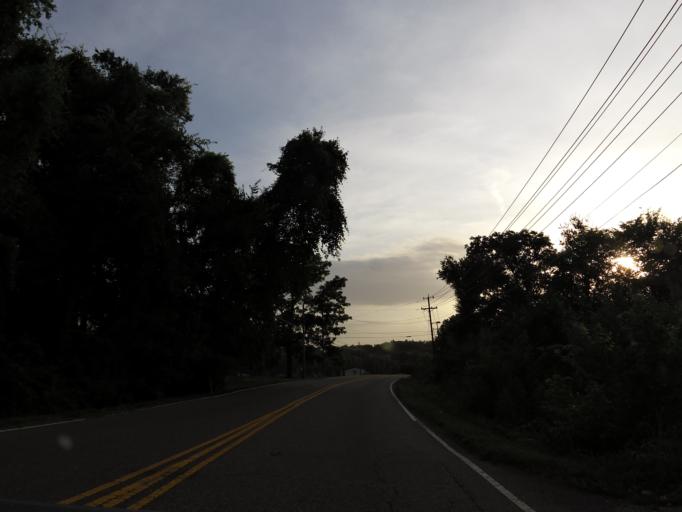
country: US
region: Tennessee
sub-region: Knox County
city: Knoxville
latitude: 35.9799
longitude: -83.8266
